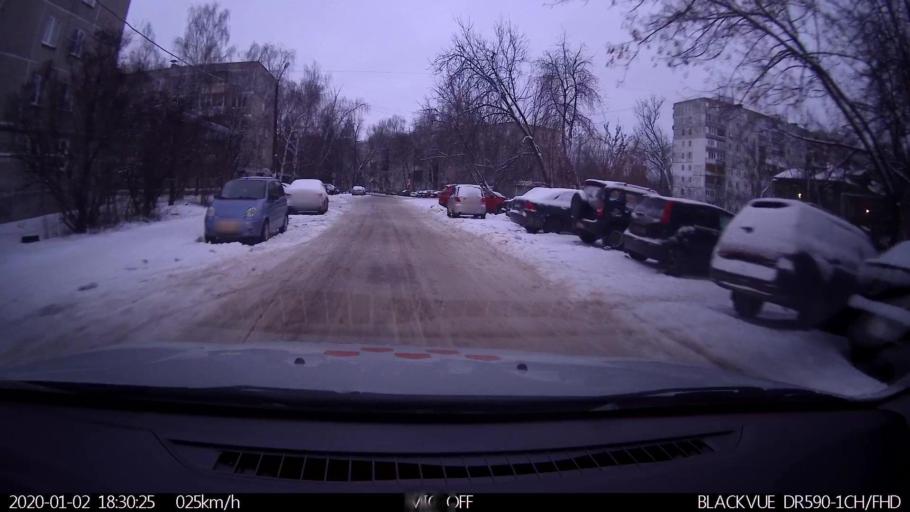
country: RU
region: Nizjnij Novgorod
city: Gorbatovka
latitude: 56.3345
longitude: 43.8367
